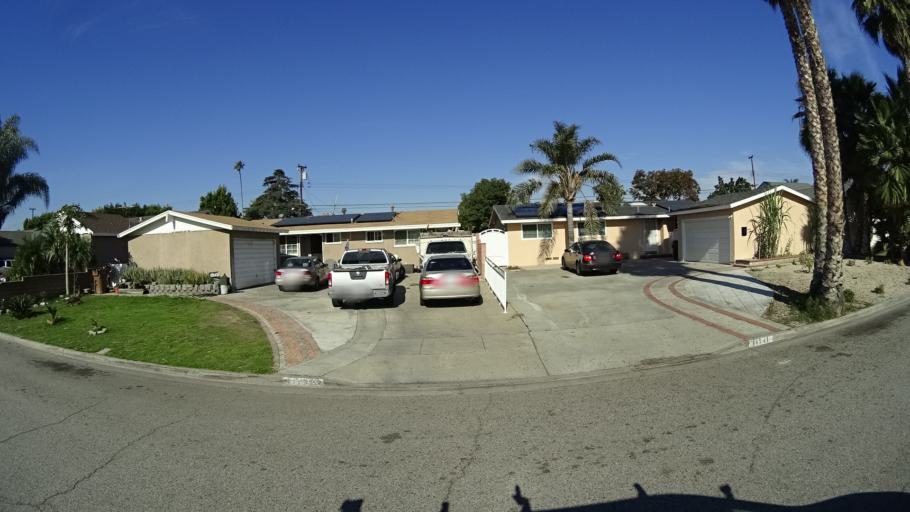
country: US
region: California
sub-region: Orange County
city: Garden Grove
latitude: 33.7863
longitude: -117.9278
